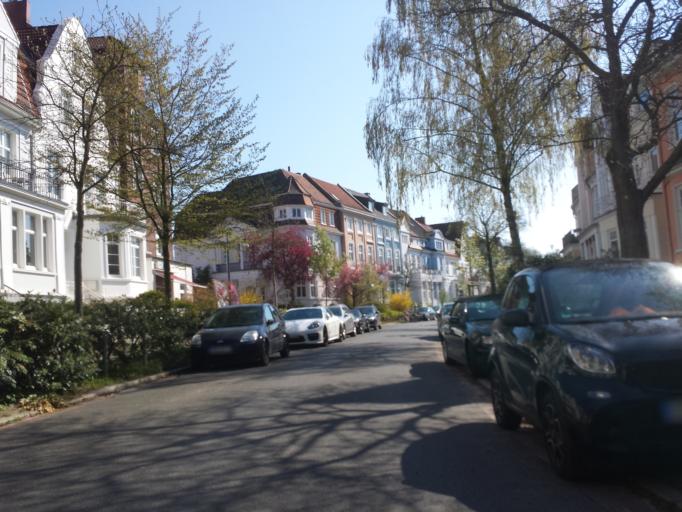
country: DE
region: Bremen
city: Bremen
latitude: 53.0810
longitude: 8.8387
